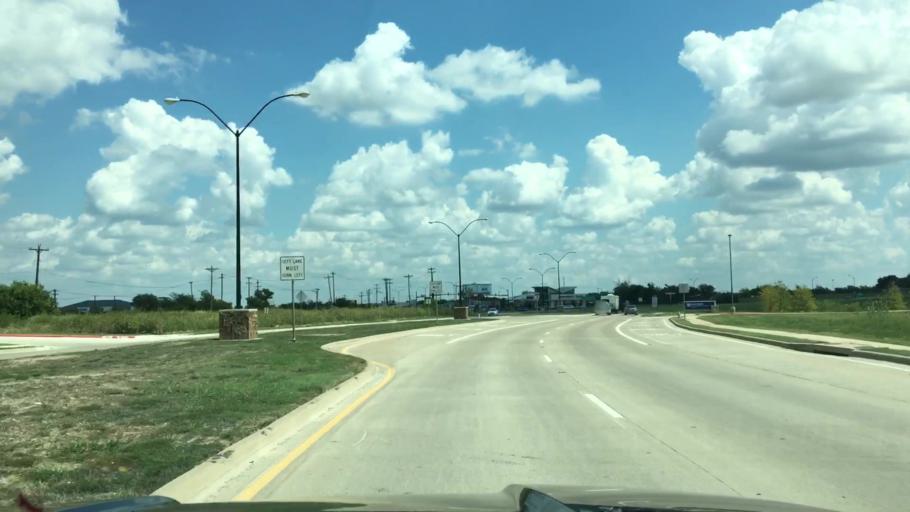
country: US
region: Texas
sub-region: Tarrant County
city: Haslet
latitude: 32.9332
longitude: -97.3106
